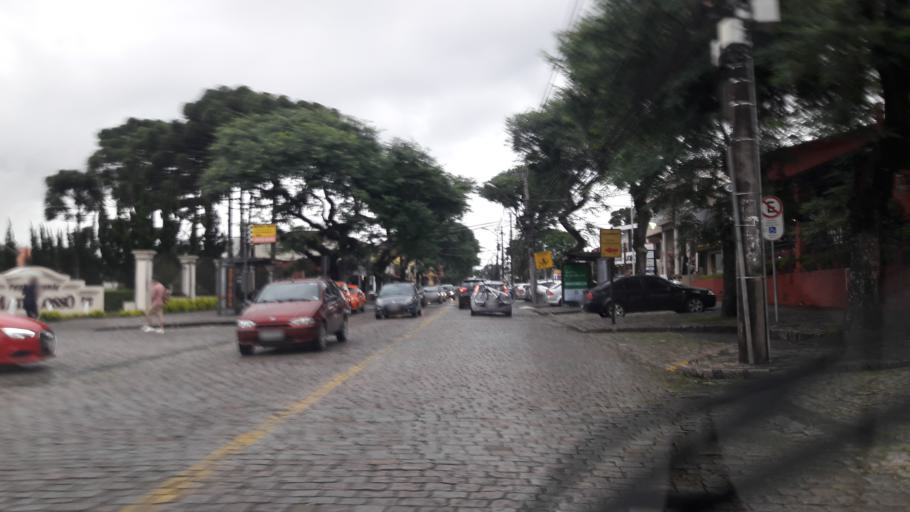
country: BR
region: Parana
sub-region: Curitiba
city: Curitiba
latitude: -25.4044
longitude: -49.3274
